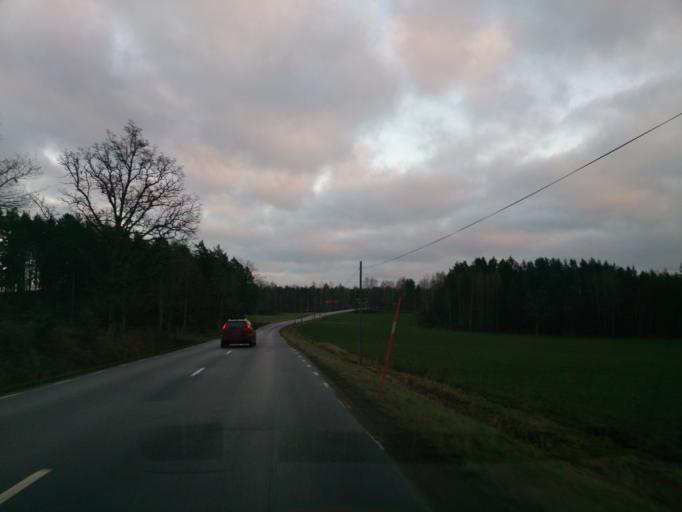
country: SE
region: OEstergoetland
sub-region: Norrkopings Kommun
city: Kimstad
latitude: 58.3902
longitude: 15.9828
